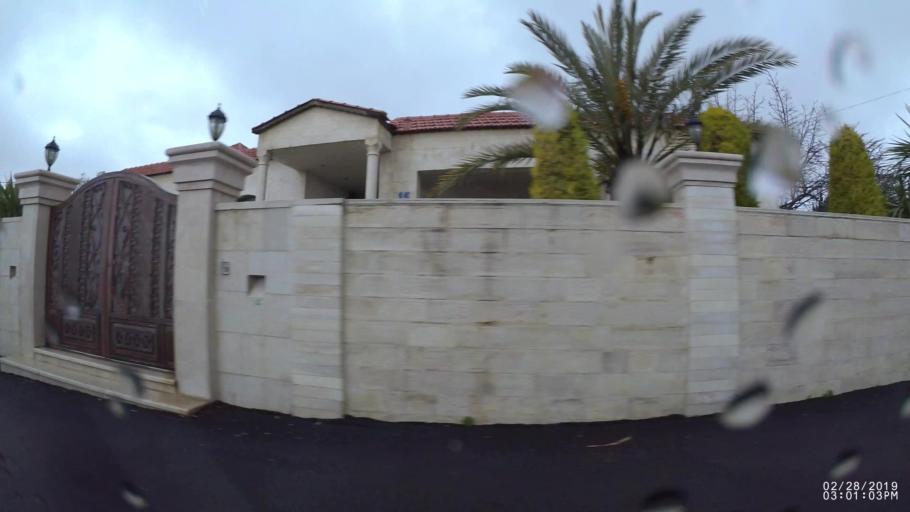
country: JO
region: Amman
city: Al Jubayhah
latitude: 32.0269
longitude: 35.8679
